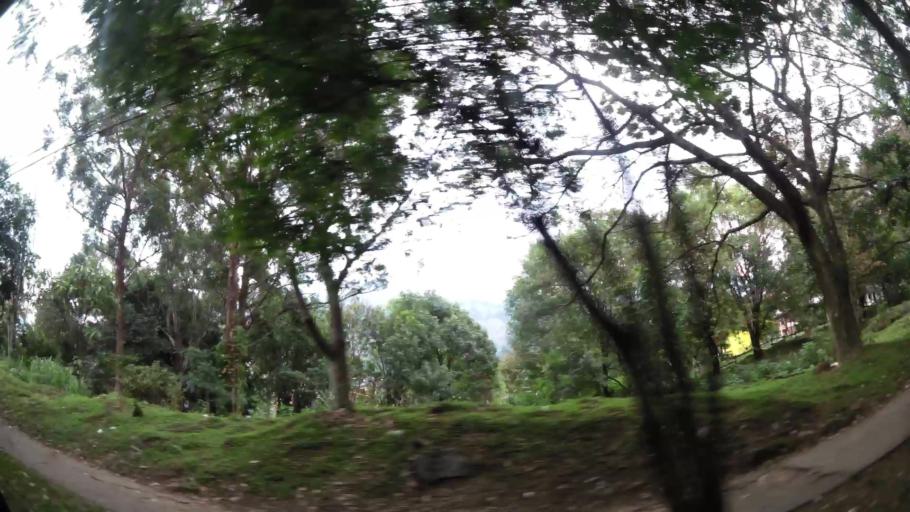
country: CO
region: Antioquia
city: Medellin
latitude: 6.2354
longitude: -75.5471
